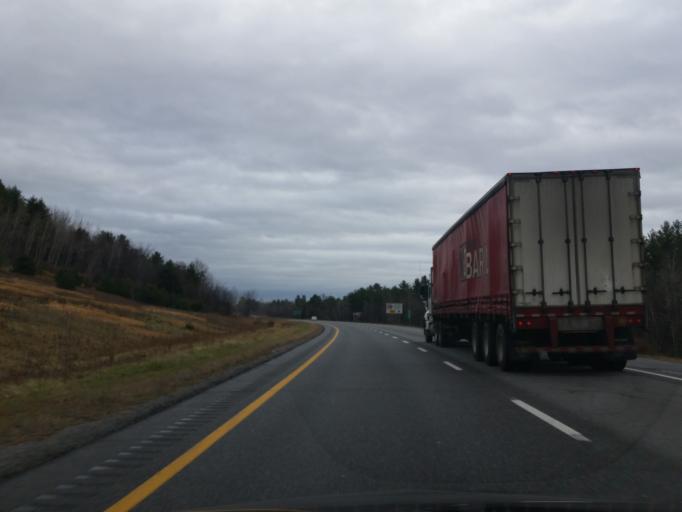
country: CA
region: Ontario
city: Clarence-Rockland
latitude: 45.5430
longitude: -75.4481
